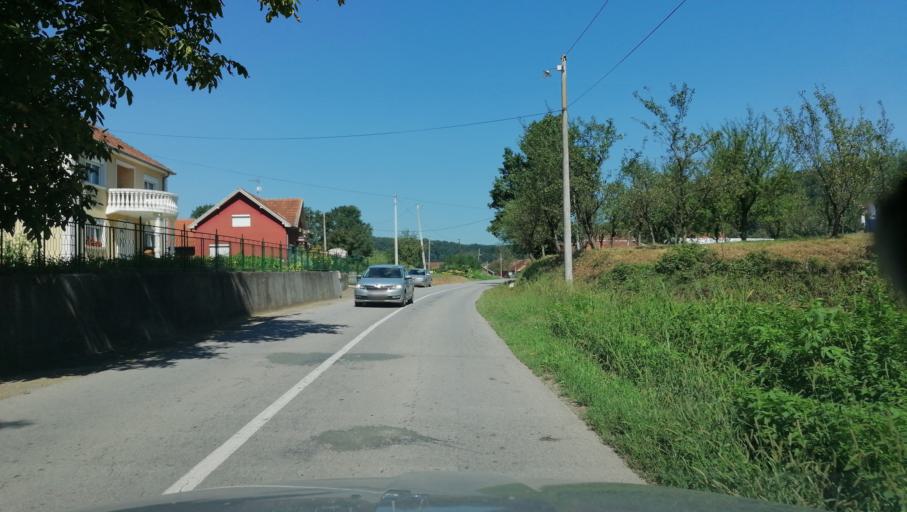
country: RS
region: Central Serbia
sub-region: Raski Okrug
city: Vrnjacka Banja
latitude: 43.6991
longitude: 20.8554
